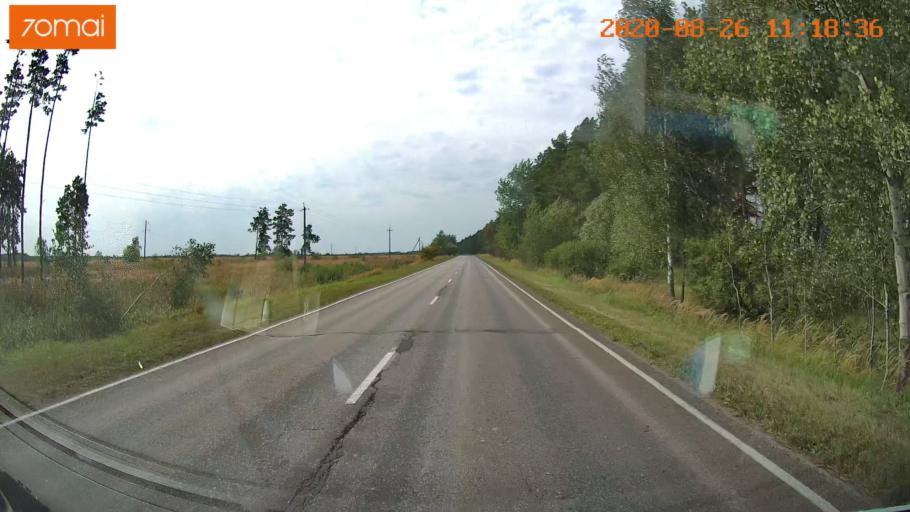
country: RU
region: Rjazan
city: Shilovo
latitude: 54.4082
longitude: 41.0943
